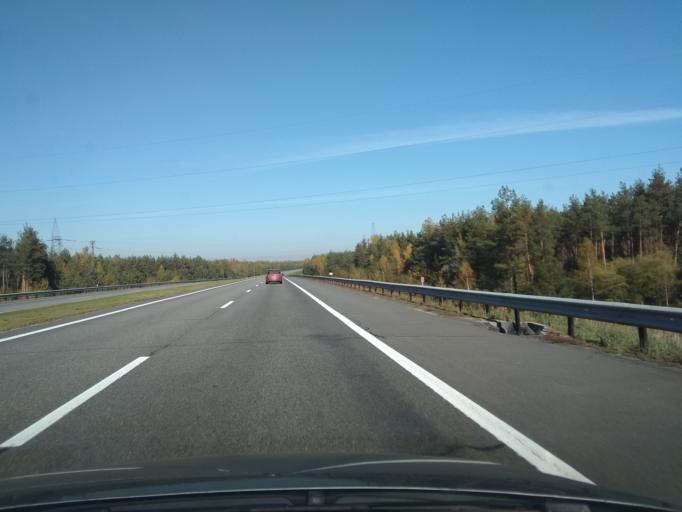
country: BY
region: Grodnenskaya
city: Zhyrovichy
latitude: 52.9145
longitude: 25.6835
